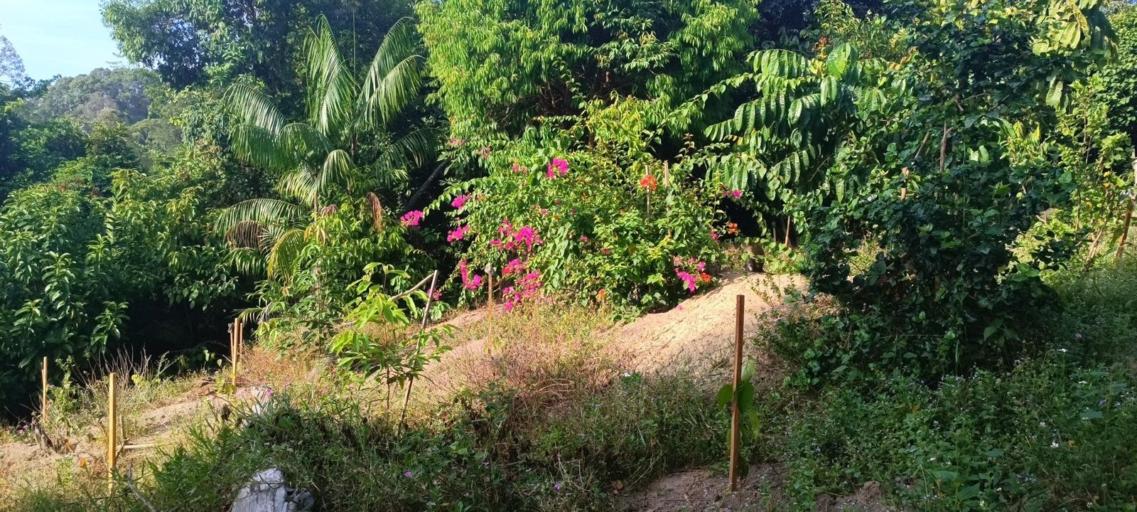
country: MY
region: Penang
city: Juru
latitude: 5.3352
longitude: 100.4123
